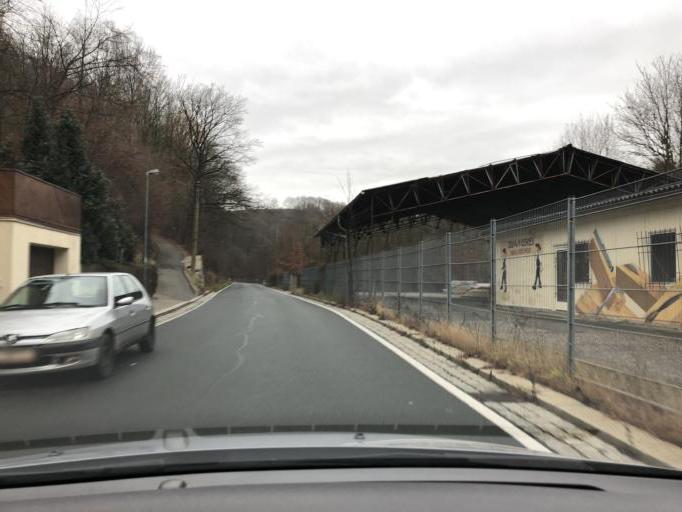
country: DE
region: Saxony
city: Rosswein
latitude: 51.0666
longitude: 13.1975
